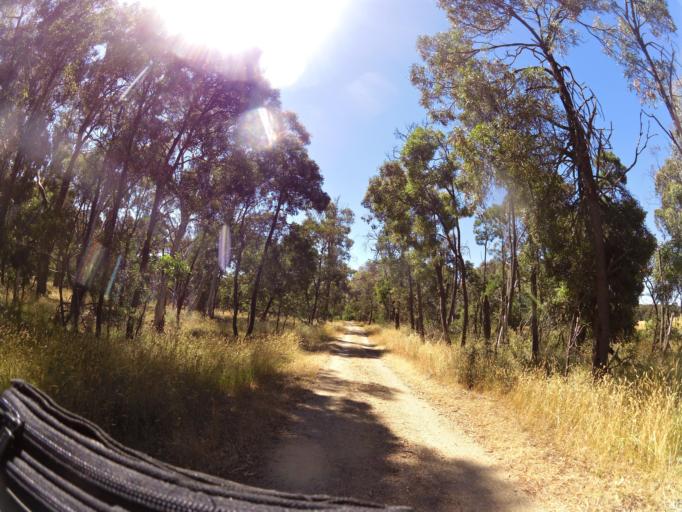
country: AU
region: Victoria
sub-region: Ballarat North
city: Delacombe
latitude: -37.6964
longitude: 143.5724
